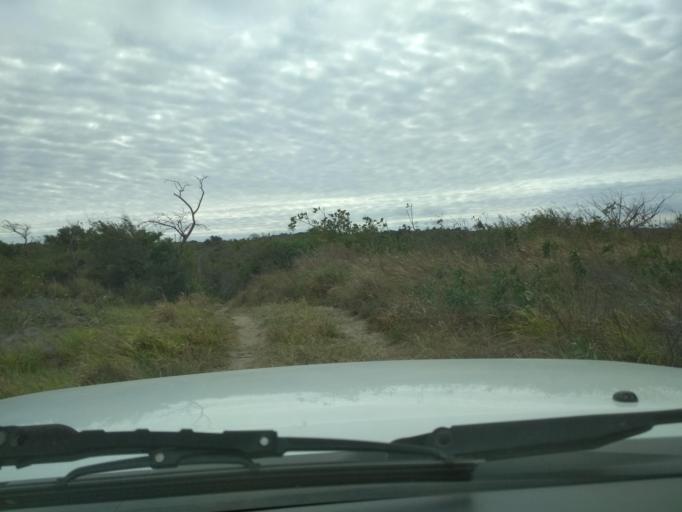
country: MX
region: Veracruz
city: Anton Lizardo
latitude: 19.0483
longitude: -95.9884
